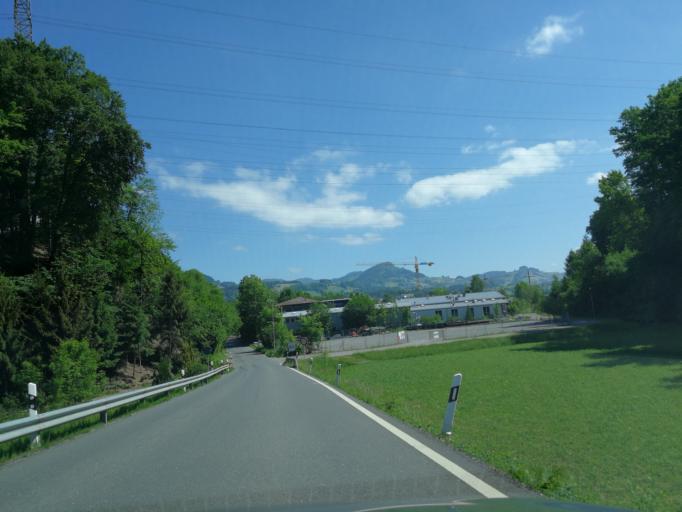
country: CH
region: Saint Gallen
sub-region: Wahlkreis See-Gaster
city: Eschenbach
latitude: 47.2331
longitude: 8.9239
